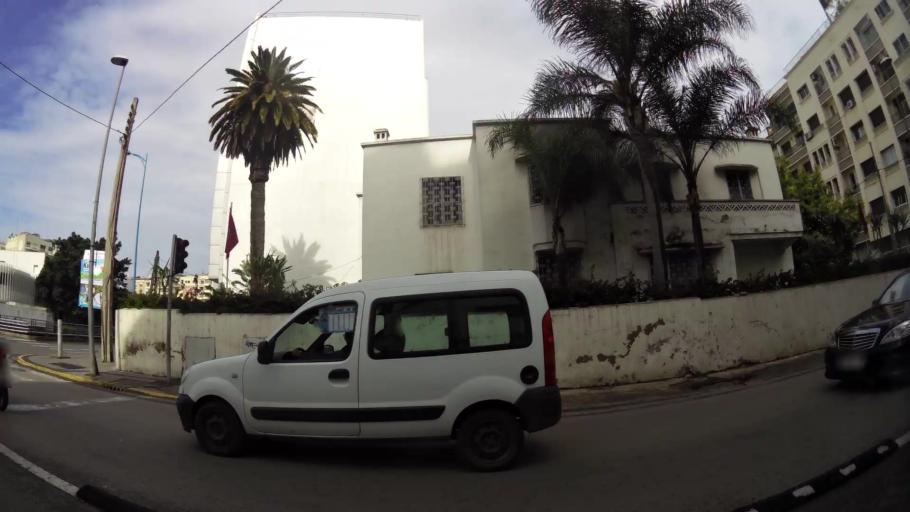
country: MA
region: Grand Casablanca
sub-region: Casablanca
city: Casablanca
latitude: 33.5839
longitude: -7.6252
